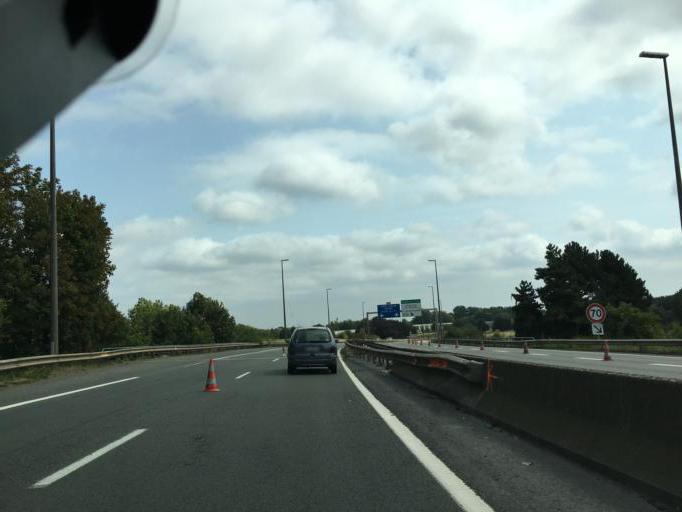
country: FR
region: Nord-Pas-de-Calais
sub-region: Departement du Pas-de-Calais
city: Lens
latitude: 50.4508
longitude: 2.8300
